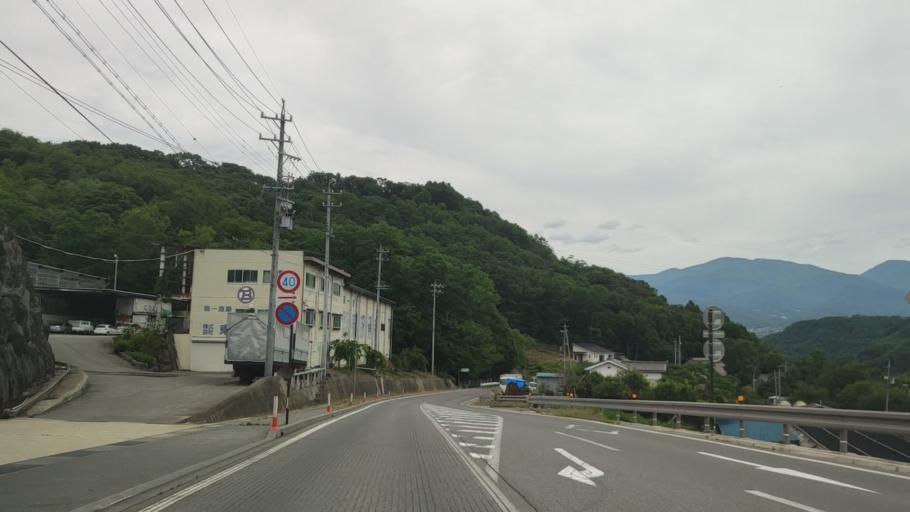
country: JP
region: Nagano
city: Kamimaruko
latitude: 36.3231
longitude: 138.3382
